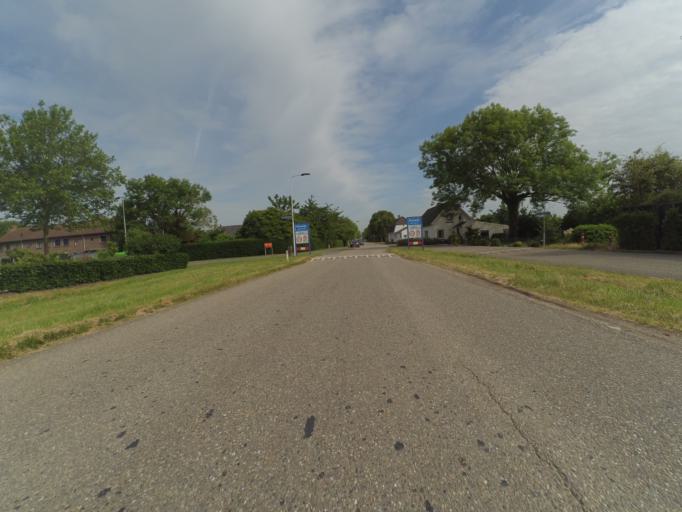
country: NL
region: Utrecht
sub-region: Gemeente Wijk bij Duurstede
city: Wijk bij Duurstede
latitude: 51.9578
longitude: 5.3585
